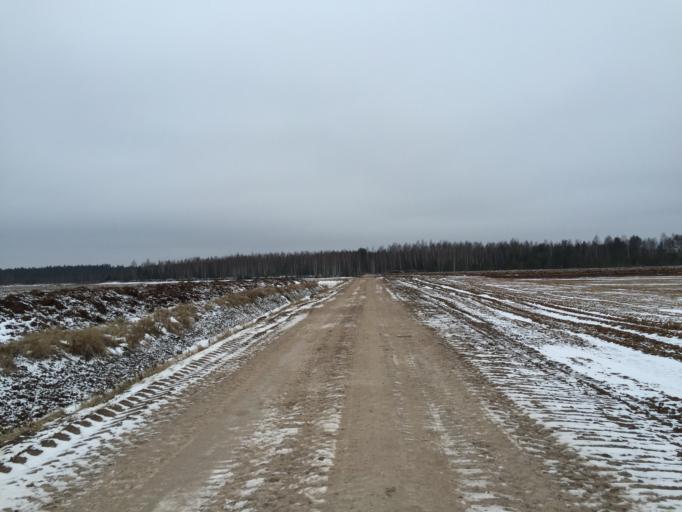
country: LV
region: Saulkrastu
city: Saulkrasti
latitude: 57.2395
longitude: 24.4952
